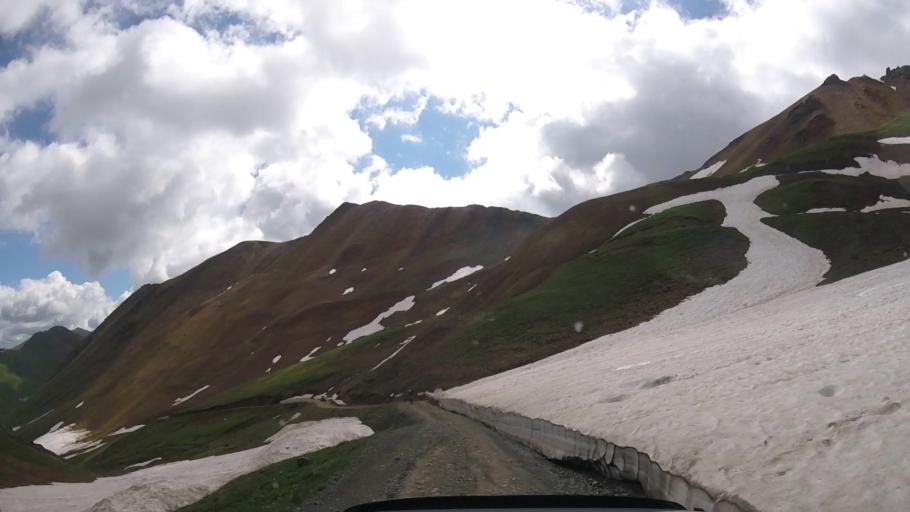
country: US
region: Colorado
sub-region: San Juan County
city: Silverton
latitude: 37.9144
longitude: -107.6149
